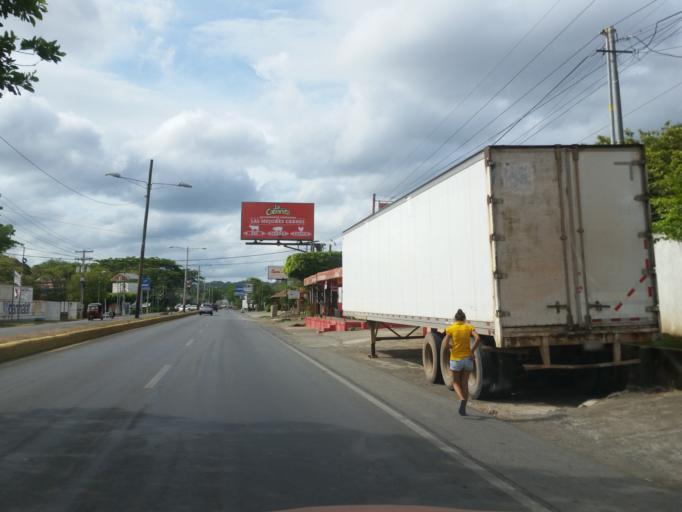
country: NI
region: Masaya
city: Ticuantepe
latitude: 12.0480
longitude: -86.1961
